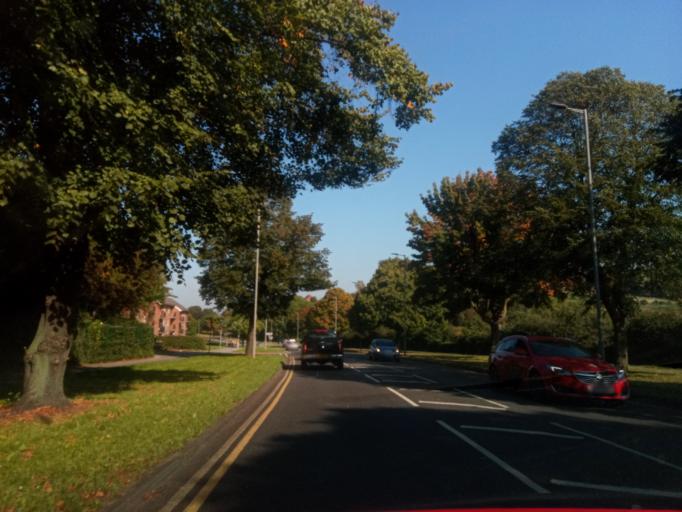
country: GB
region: England
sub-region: Rotherham
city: Rawmarsh
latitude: 53.4404
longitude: -1.3220
